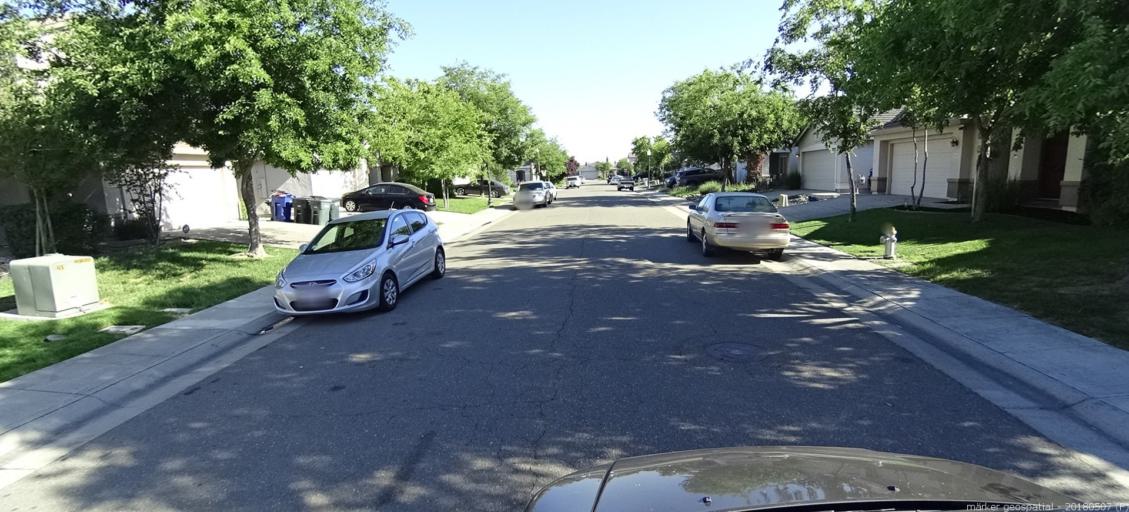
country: US
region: California
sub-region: Sacramento County
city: Rio Linda
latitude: 38.6733
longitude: -121.4939
